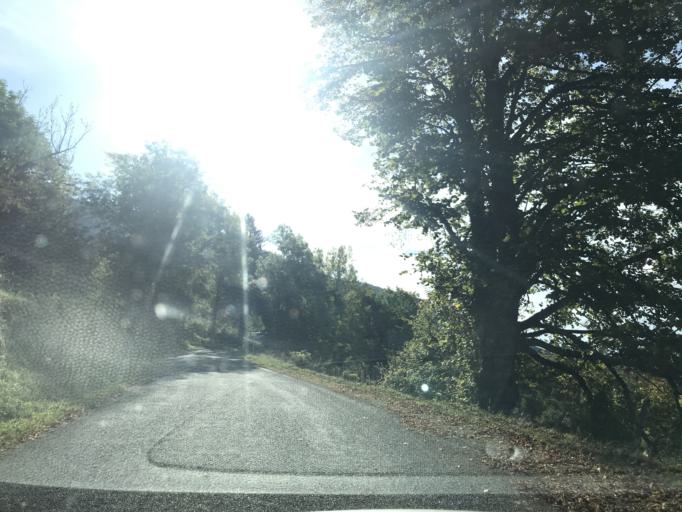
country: FR
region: Rhone-Alpes
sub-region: Departement de la Savoie
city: Novalaise
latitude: 45.6351
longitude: 5.7995
